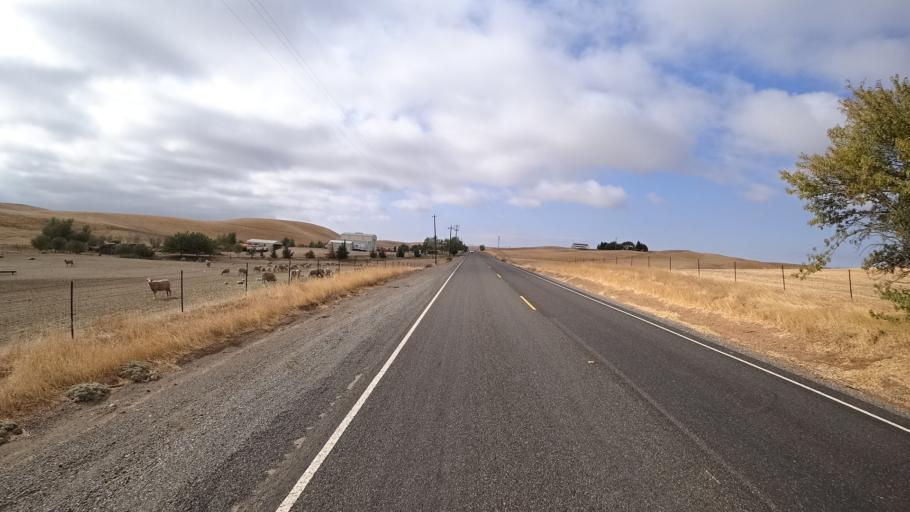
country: US
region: California
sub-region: Yolo County
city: Dunnigan
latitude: 38.7881
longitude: -121.9187
